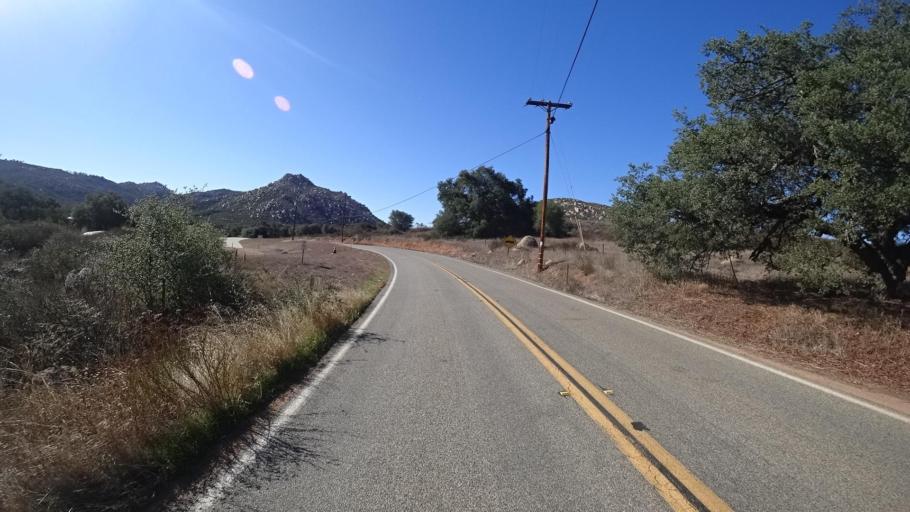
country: US
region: California
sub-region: San Diego County
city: Jamul
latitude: 32.6839
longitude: -116.7541
